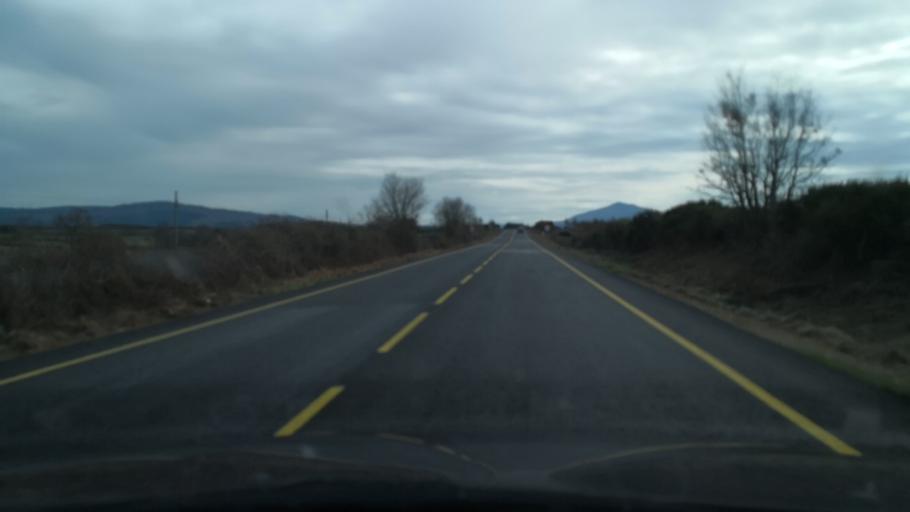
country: ES
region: Castille and Leon
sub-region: Provincia de Salamanca
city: Villasrubias
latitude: 40.3578
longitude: -6.6263
